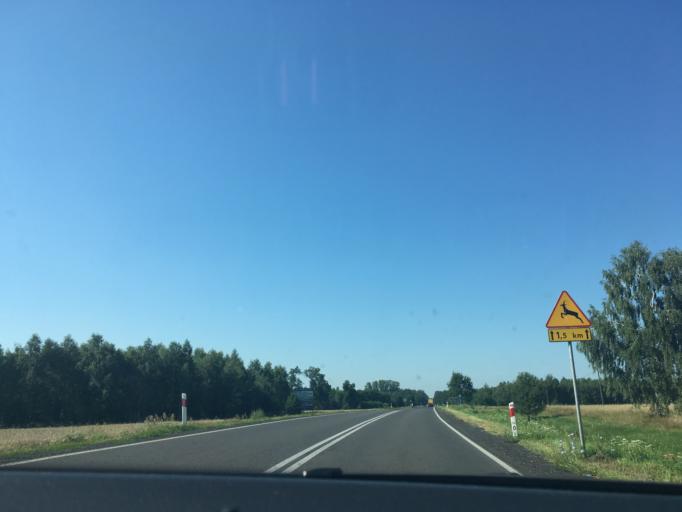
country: PL
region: Lublin Voivodeship
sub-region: Powiat lubartowski
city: Kock
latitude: 51.6762
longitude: 22.4846
